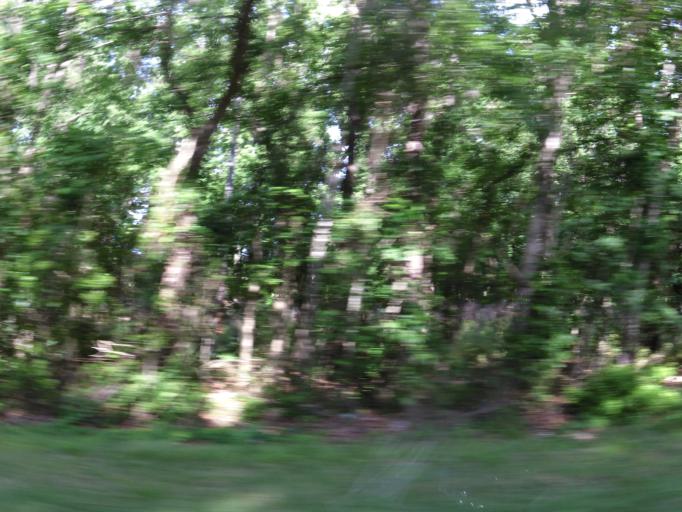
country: US
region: South Carolina
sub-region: Allendale County
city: Fairfax
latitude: 32.8999
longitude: -81.2378
